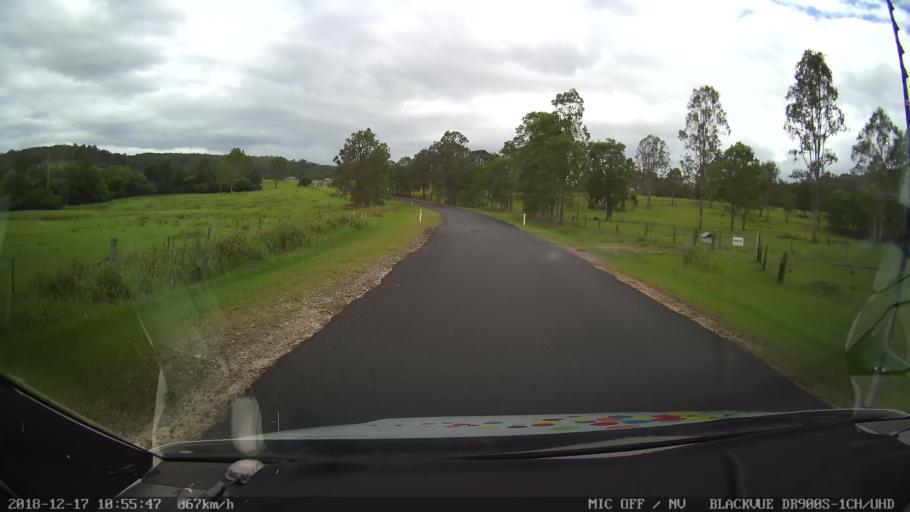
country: AU
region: New South Wales
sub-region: Richmond Valley
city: Casino
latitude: -28.8266
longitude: 152.5831
